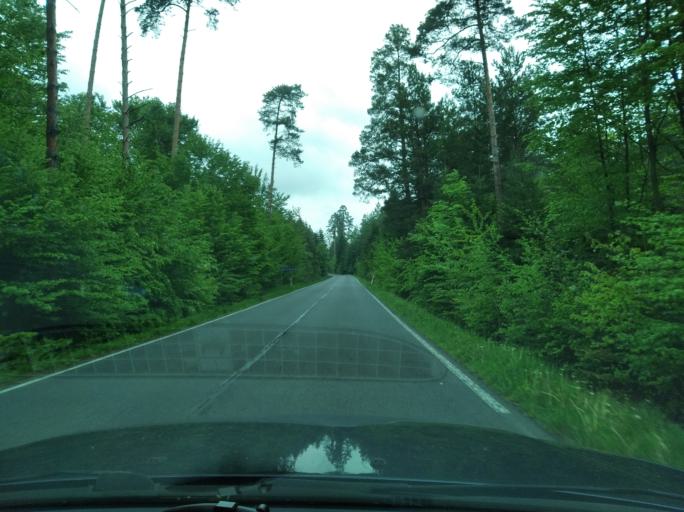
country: PL
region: Subcarpathian Voivodeship
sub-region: Powiat kolbuszowski
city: Kolbuszowa
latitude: 50.1671
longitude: 21.7597
